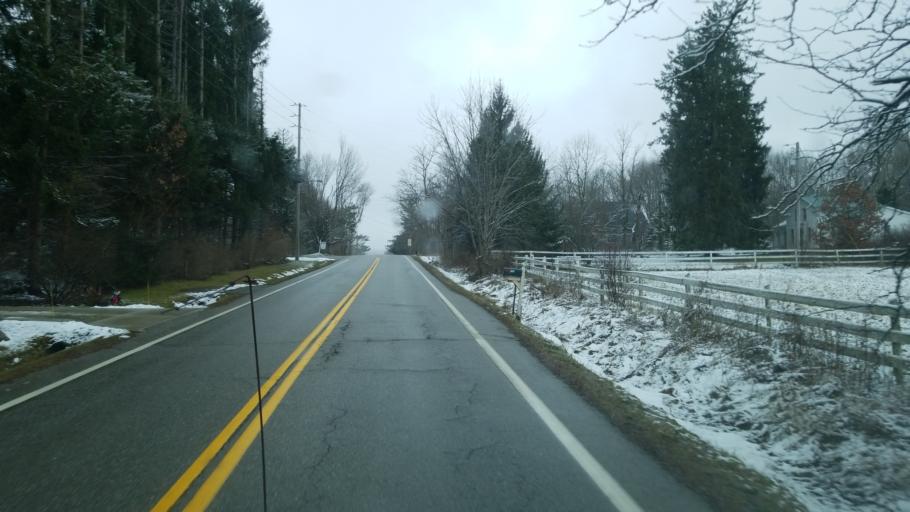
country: US
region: Ohio
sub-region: Portage County
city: Garrettsville
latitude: 41.3099
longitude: -81.1108
